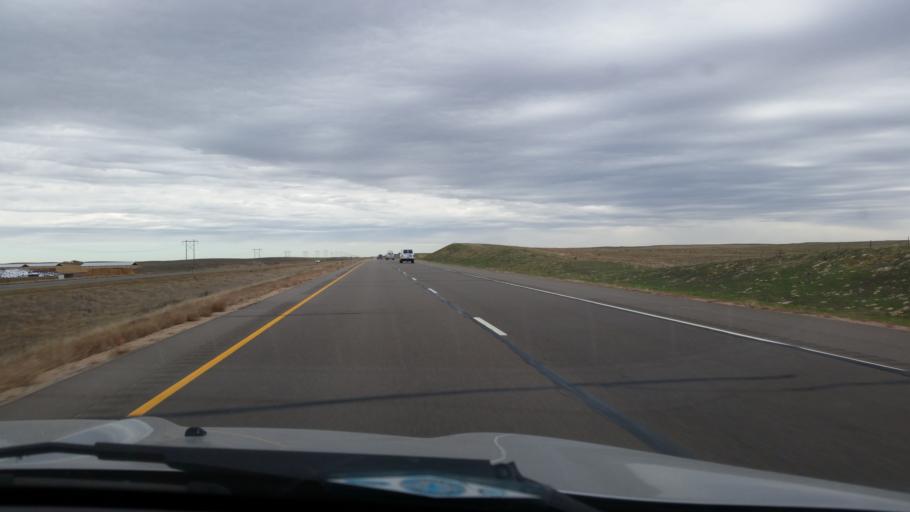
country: US
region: Colorado
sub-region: Morgan County
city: Brush
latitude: 40.3351
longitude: -103.4692
